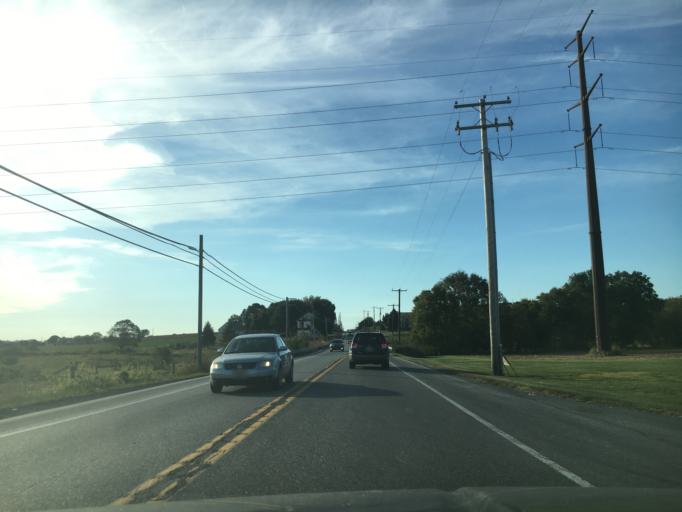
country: US
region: Pennsylvania
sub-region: Lancaster County
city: Ephrata
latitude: 40.1571
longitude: -76.1343
